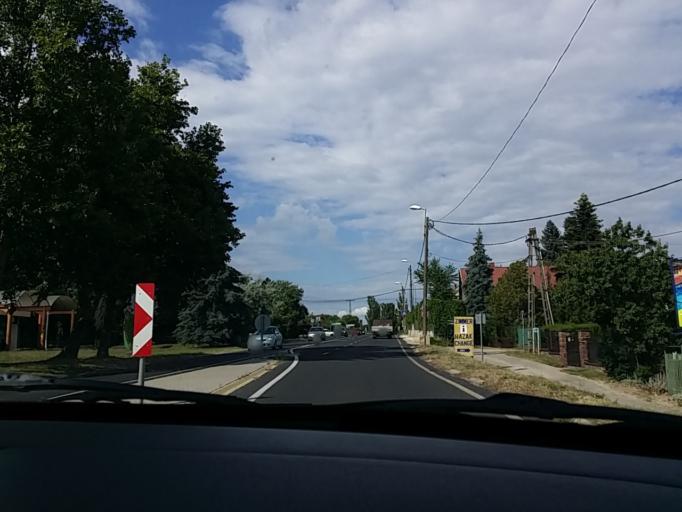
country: HU
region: Veszprem
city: Zanka
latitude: 46.8717
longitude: 17.6825
